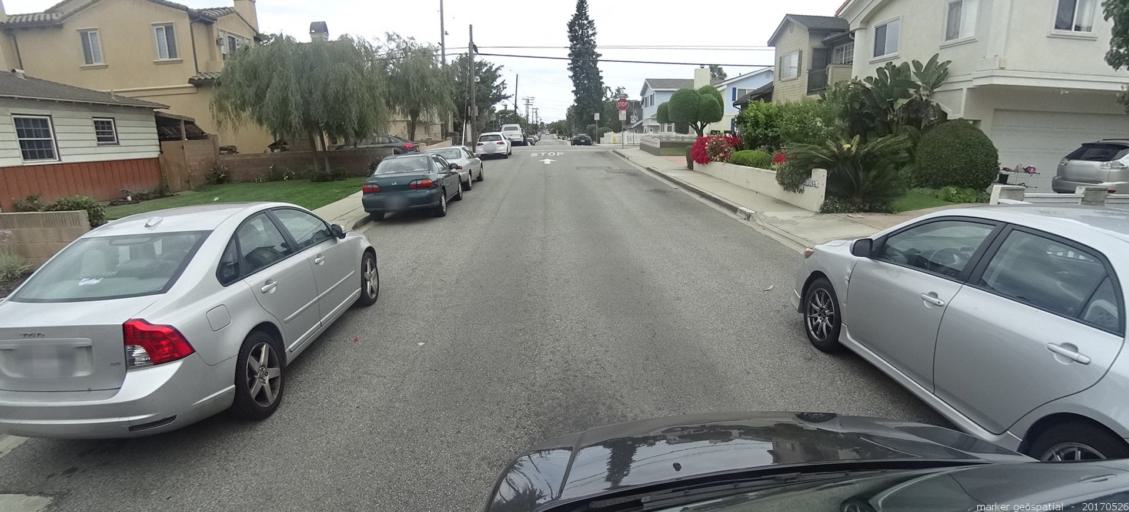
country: US
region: California
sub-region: Los Angeles County
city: Lawndale
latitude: 33.8747
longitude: -118.3723
